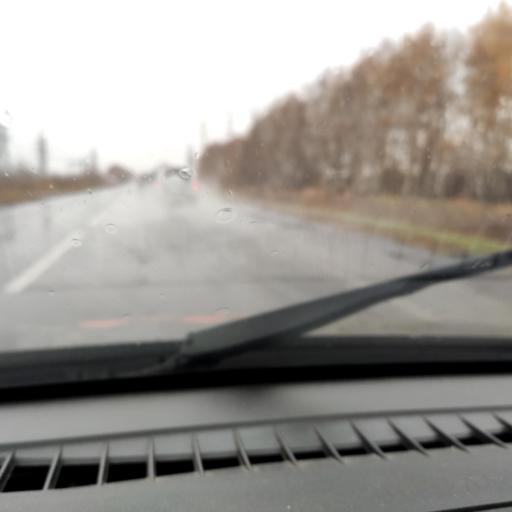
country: RU
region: Samara
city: Tol'yatti
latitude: 53.5842
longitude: 49.3334
